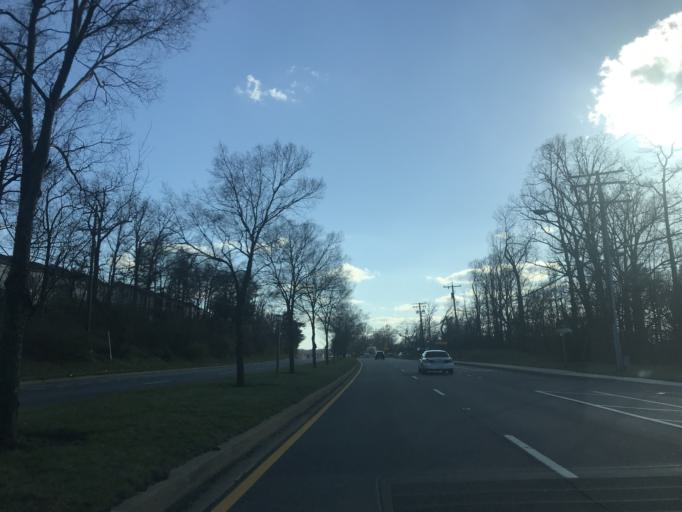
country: US
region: Maryland
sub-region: Prince George's County
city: Peppermill Village
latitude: 38.9133
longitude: -76.8877
